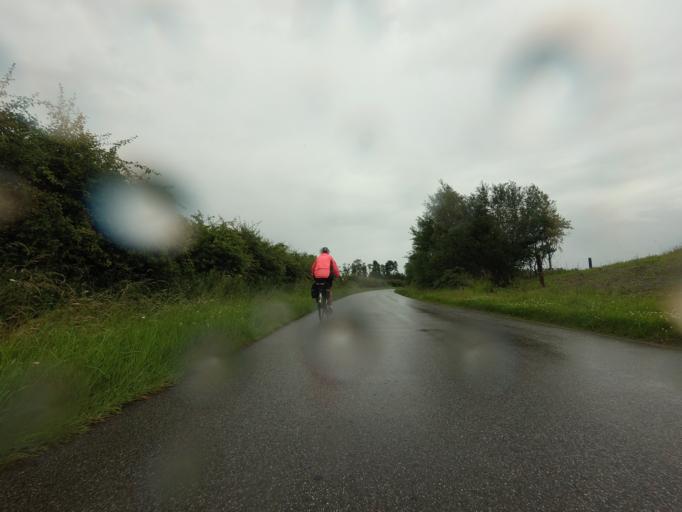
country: GB
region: Scotland
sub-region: Moray
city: Fochabers
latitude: 57.6613
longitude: -3.0659
